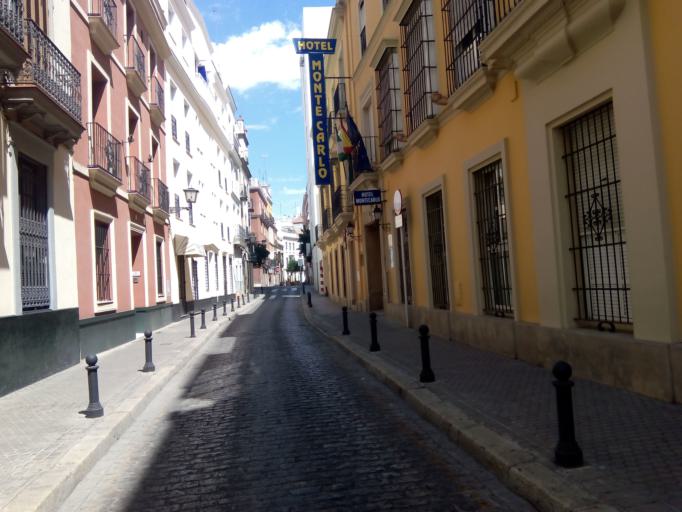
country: ES
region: Andalusia
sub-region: Provincia de Sevilla
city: Sevilla
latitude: 37.3898
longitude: -6.0000
